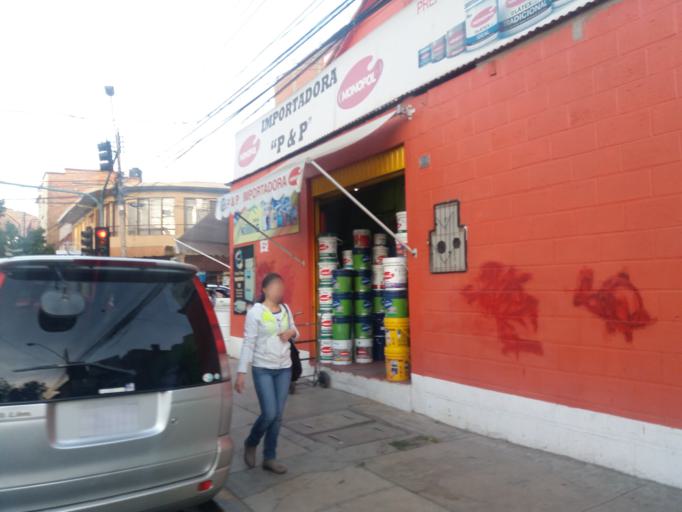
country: BO
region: Cochabamba
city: Cochabamba
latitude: -17.3885
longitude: -66.1542
